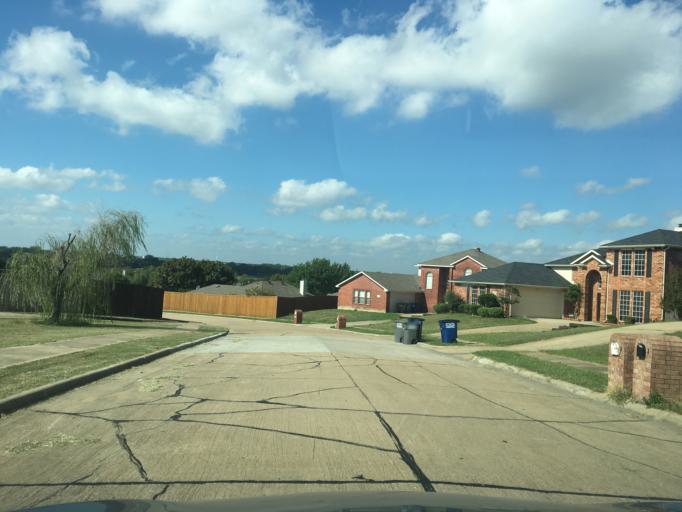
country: US
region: Texas
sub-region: Dallas County
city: Sachse
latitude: 32.9586
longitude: -96.5861
